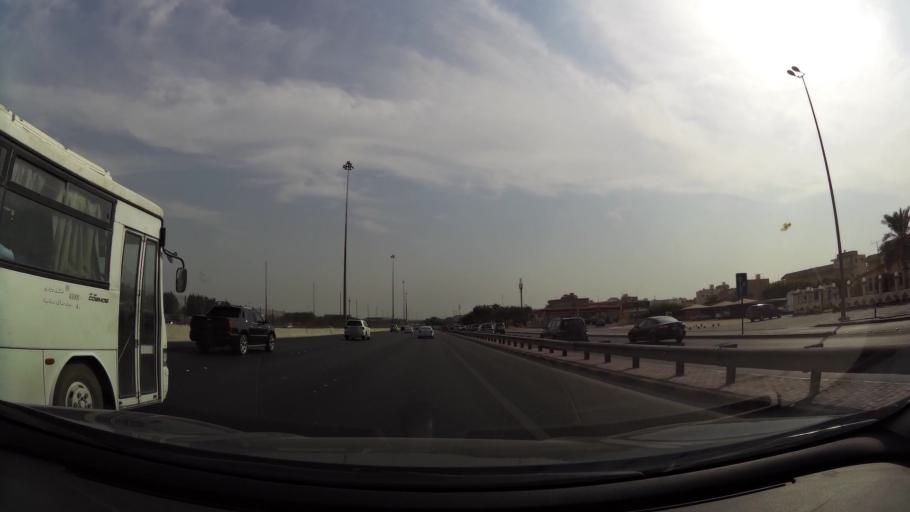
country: KW
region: Al Farwaniyah
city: Janub as Surrah
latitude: 29.2935
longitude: 47.9821
